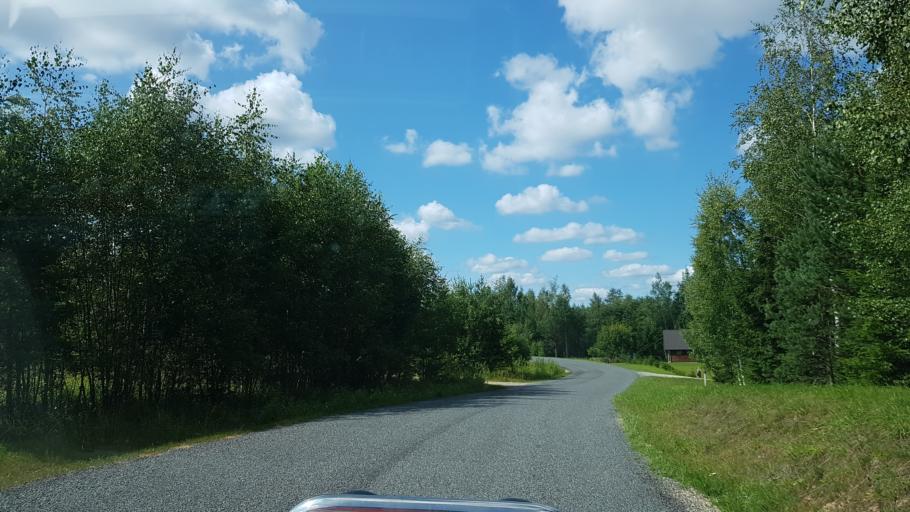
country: EE
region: Vorumaa
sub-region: Voru linn
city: Voru
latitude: 57.7294
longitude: 27.2383
